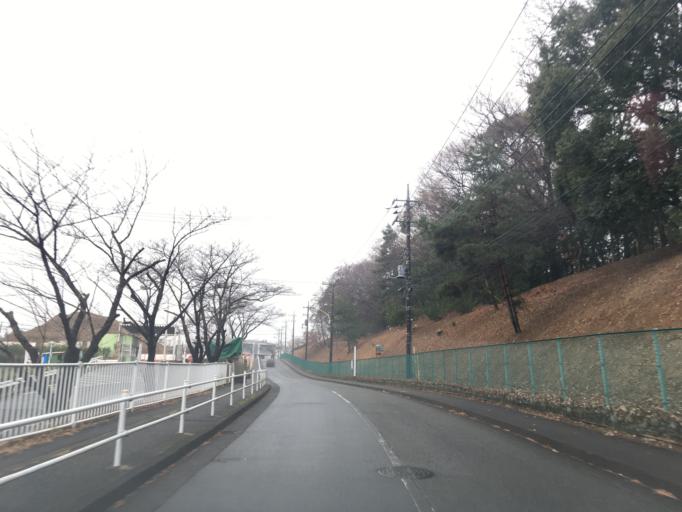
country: JP
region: Tokyo
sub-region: Machida-shi
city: Machida
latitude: 35.5880
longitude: 139.4104
